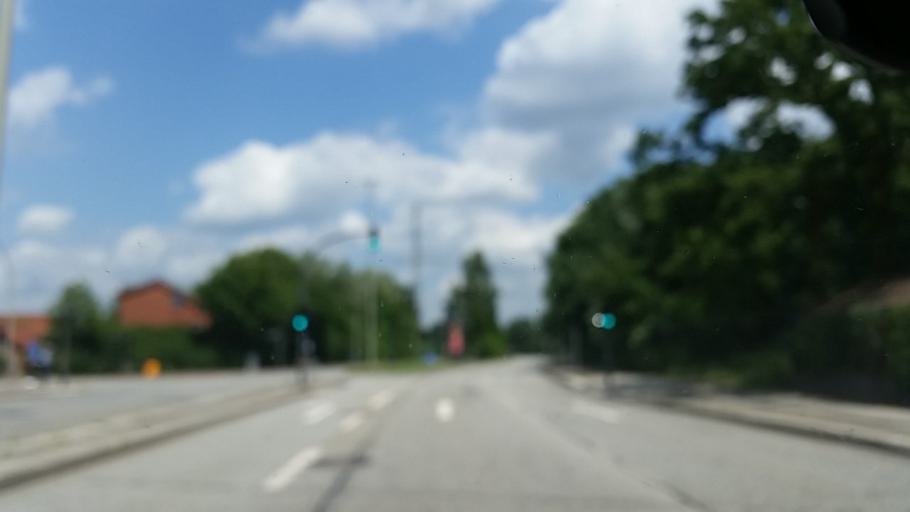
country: DE
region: Hamburg
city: Bergedorf
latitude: 53.4762
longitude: 10.1779
